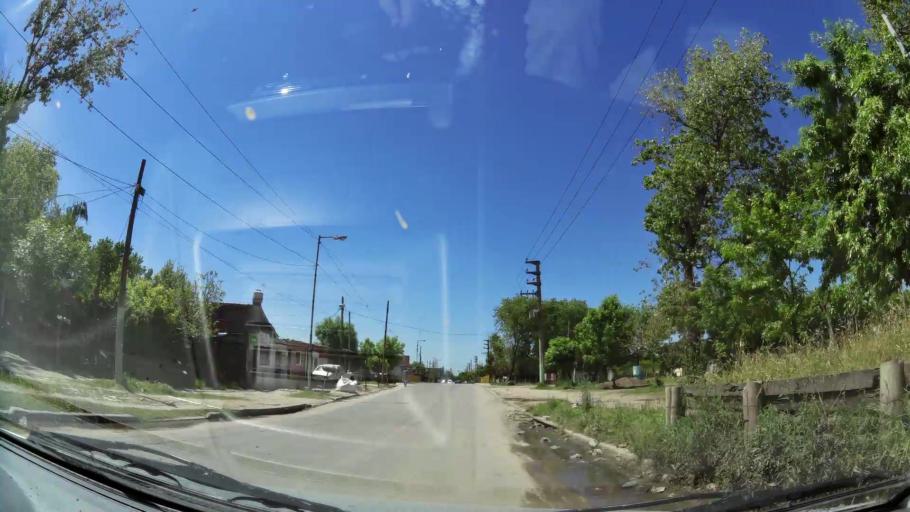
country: AR
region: Buenos Aires
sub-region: Partido de Quilmes
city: Quilmes
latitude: -34.7249
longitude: -58.3150
